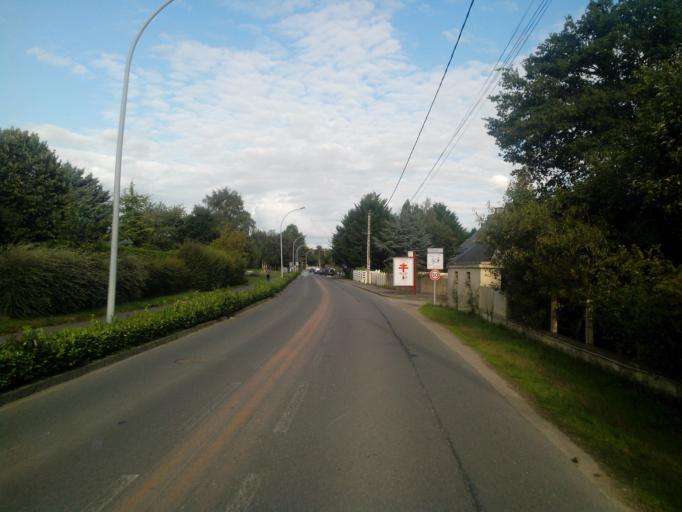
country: FR
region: Brittany
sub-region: Departement d'Ille-et-Vilaine
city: Montfort-sur-Meu
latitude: 48.1379
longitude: -1.9667
